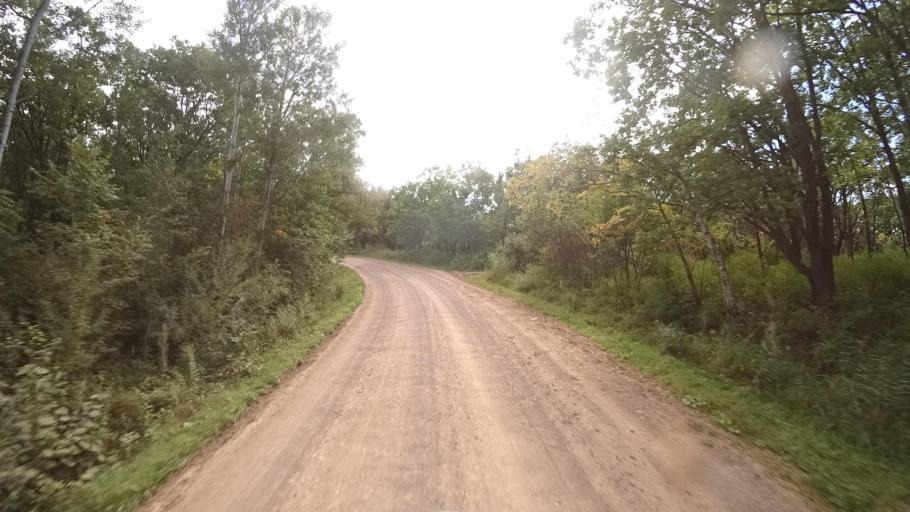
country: RU
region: Primorskiy
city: Dostoyevka
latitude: 44.3518
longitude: 133.5199
